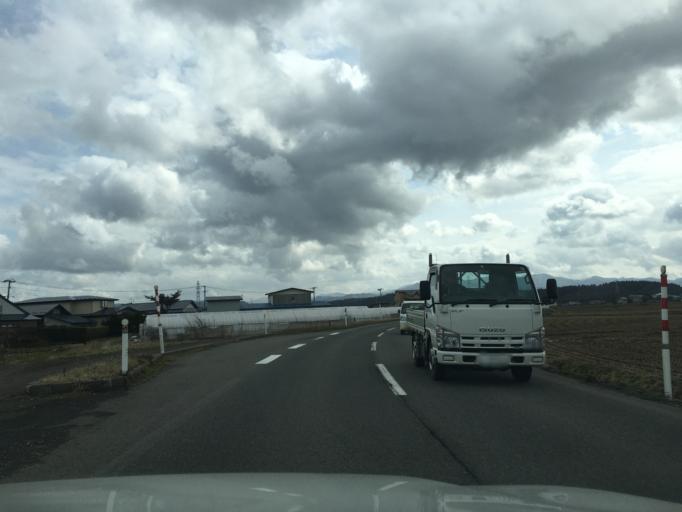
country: JP
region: Akita
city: Tenno
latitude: 39.9361
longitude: 140.0916
